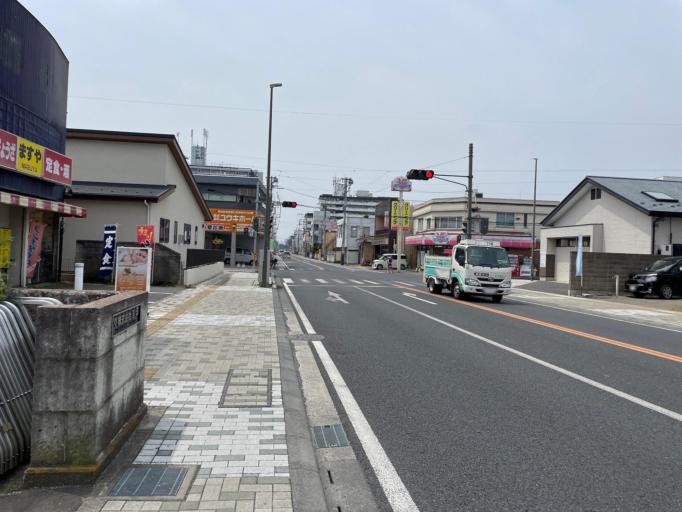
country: JP
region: Tochigi
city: Oyama
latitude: 36.3093
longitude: 139.8016
